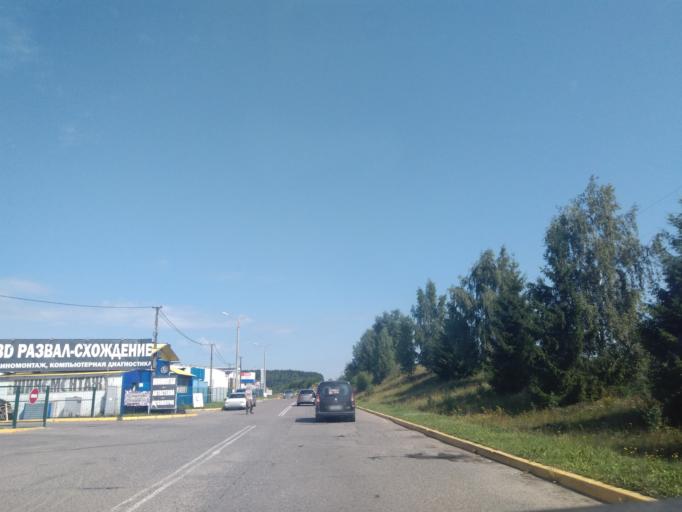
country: BY
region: Minsk
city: Malinovka
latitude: 53.8549
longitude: 27.4268
